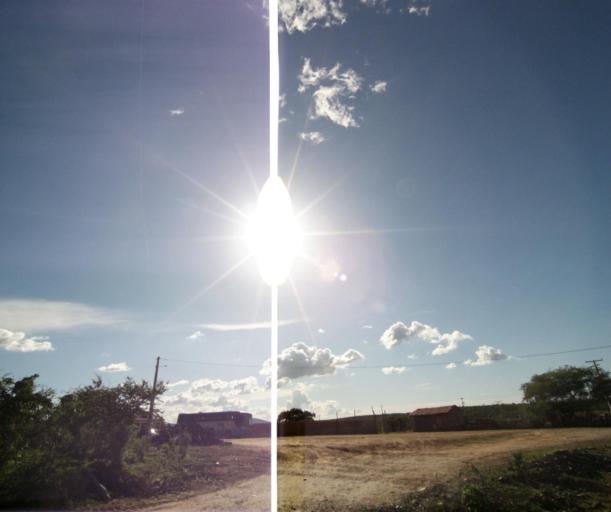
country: BR
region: Bahia
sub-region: Tanhacu
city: Tanhacu
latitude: -14.1831
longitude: -41.0123
